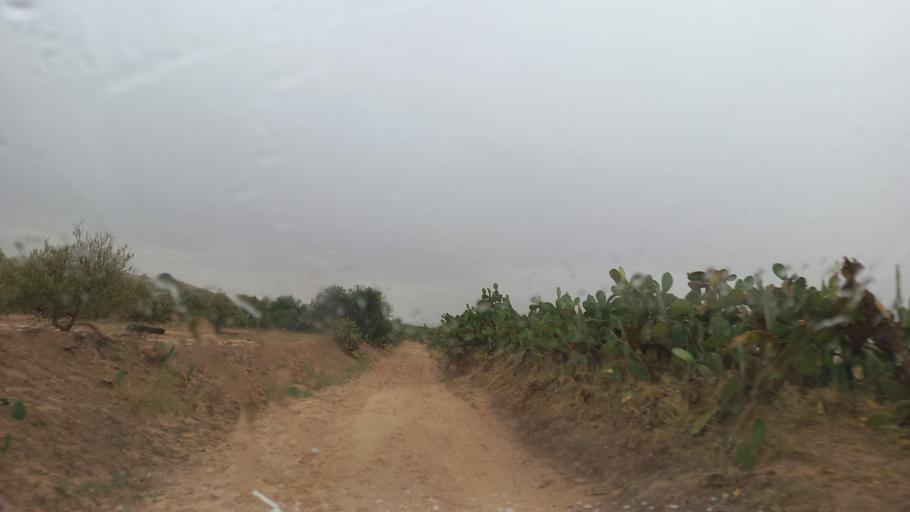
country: TN
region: Al Qasrayn
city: Kasserine
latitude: 35.2732
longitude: 8.9422
